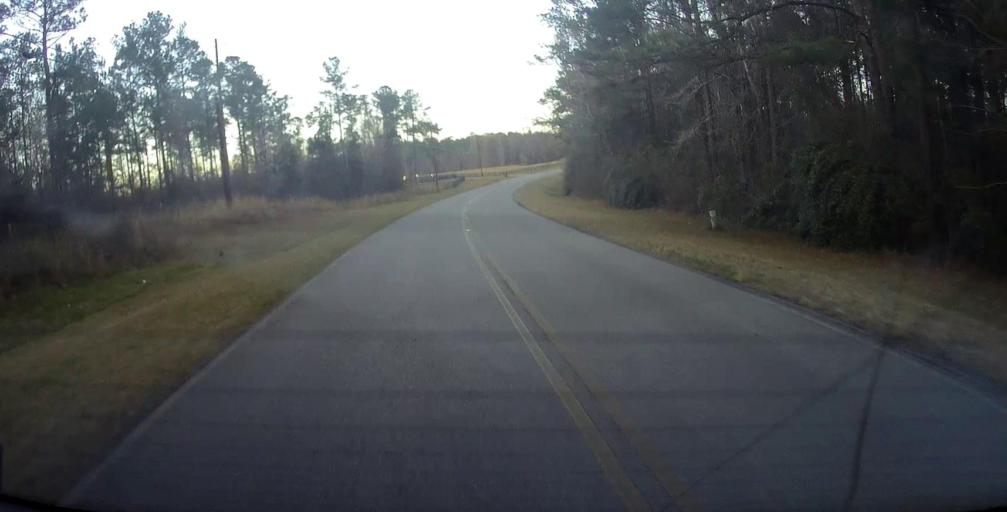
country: US
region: Georgia
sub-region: Harris County
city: Hamilton
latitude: 32.6156
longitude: -84.8217
